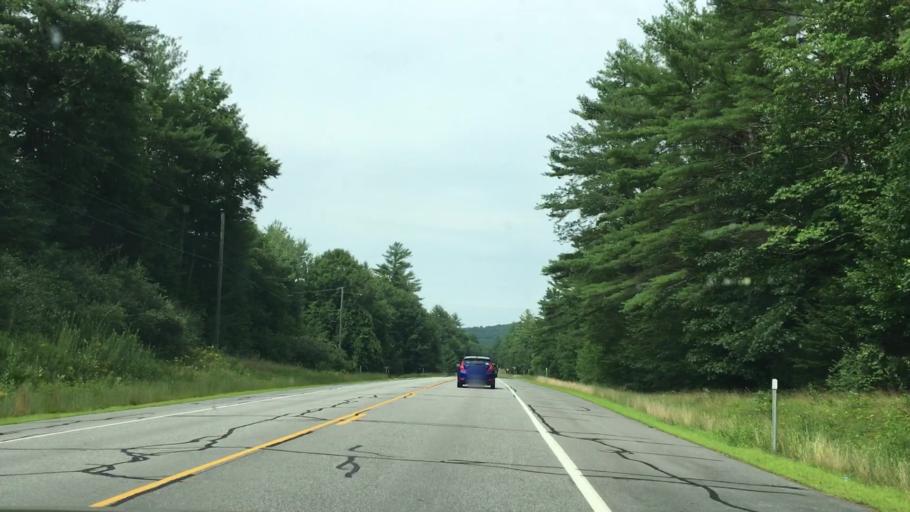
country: US
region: New Hampshire
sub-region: Hillsborough County
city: Antrim
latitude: 43.0552
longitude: -71.9224
